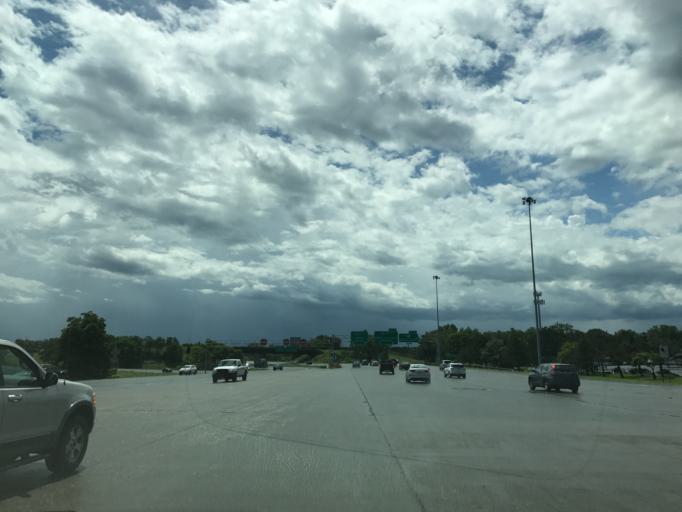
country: US
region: New York
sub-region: Albany County
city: McKownville
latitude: 42.6982
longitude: -73.8436
